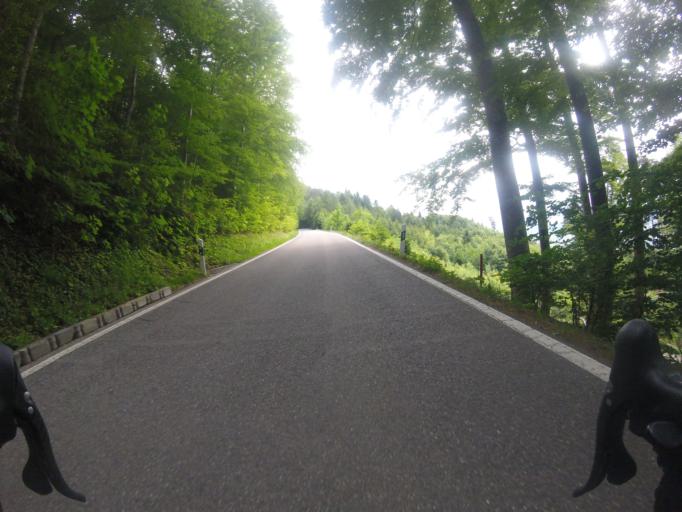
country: CH
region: Bern
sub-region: Bern-Mittelland District
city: Toffen
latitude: 46.8704
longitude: 7.5089
